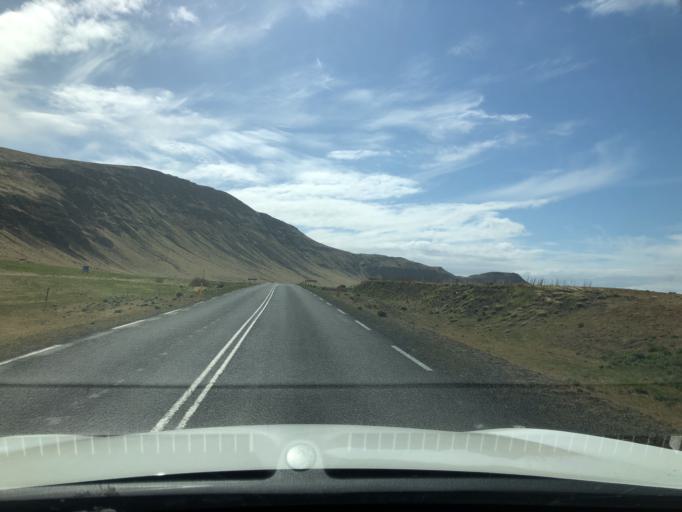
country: IS
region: Capital Region
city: Mosfellsbaer
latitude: 64.2998
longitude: -21.7900
